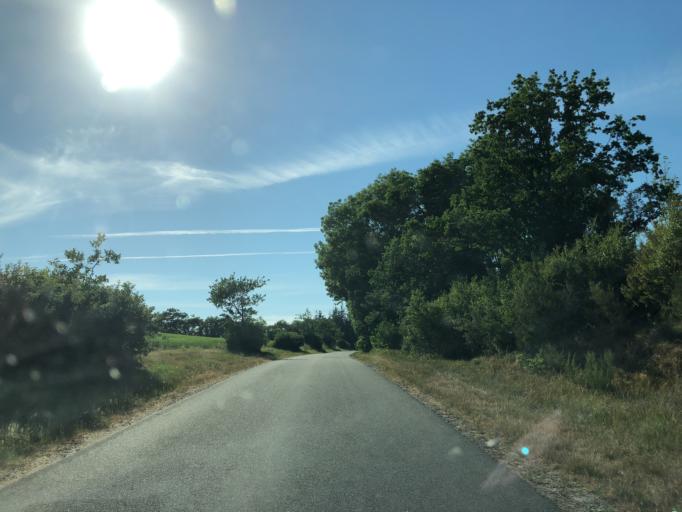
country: DK
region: Central Jutland
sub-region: Holstebro Kommune
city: Ulfborg
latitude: 56.3197
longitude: 8.3778
